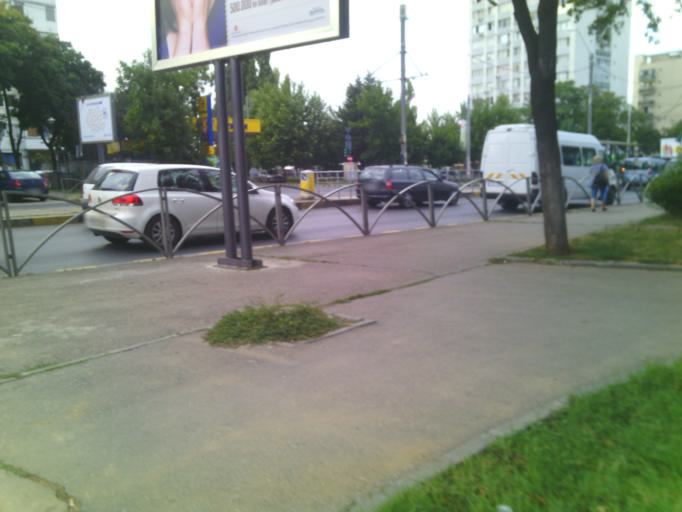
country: RO
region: Bucuresti
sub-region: Municipiul Bucuresti
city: Bucuresti
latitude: 44.3887
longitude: 26.0919
